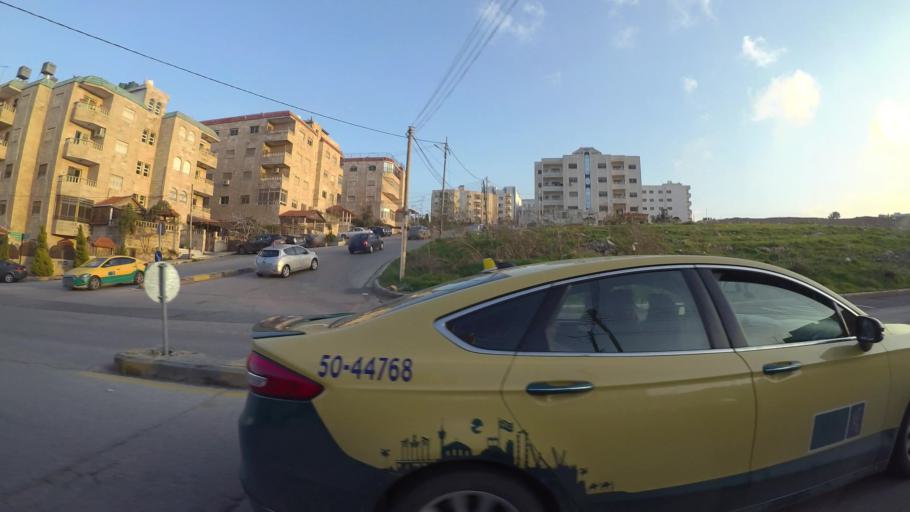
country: JO
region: Amman
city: Amman
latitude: 31.9915
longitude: 35.9535
